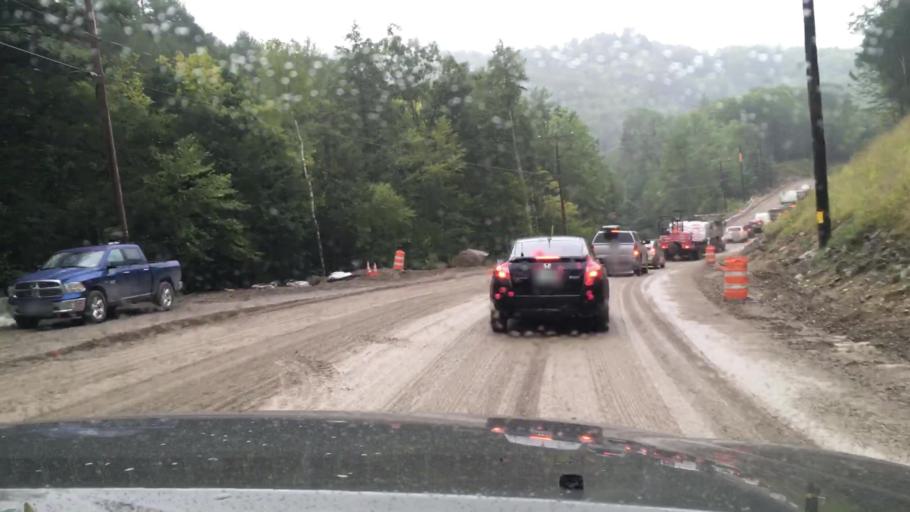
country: US
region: New Hampshire
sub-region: Cheshire County
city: Marlborough
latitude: 42.9732
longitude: -72.2064
